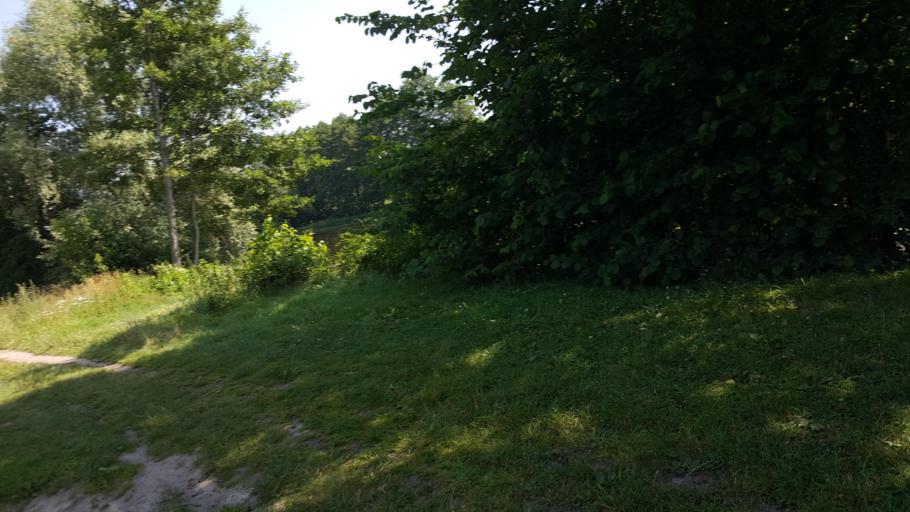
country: BY
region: Brest
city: Zhabinka
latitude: 52.1873
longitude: 24.0227
